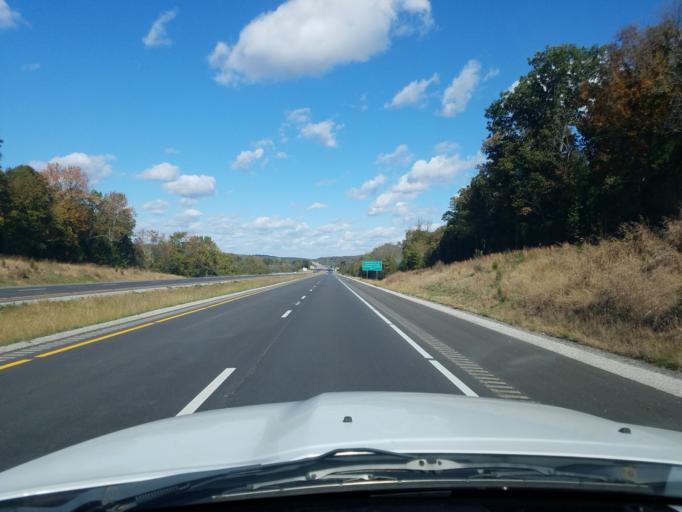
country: US
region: Kentucky
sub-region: Warren County
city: Bowling Green
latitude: 36.9728
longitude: -86.4999
